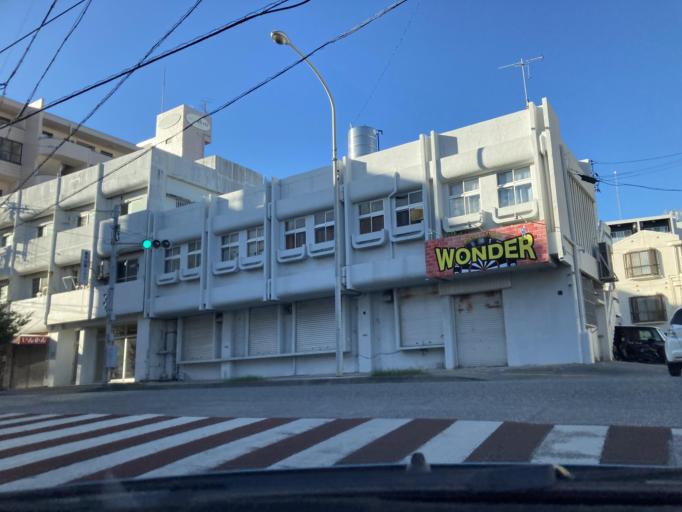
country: JP
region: Okinawa
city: Naha-shi
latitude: 26.2100
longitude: 127.6985
